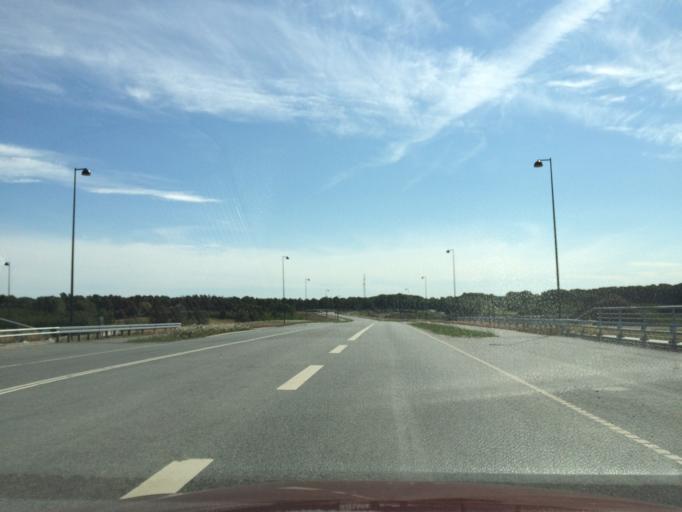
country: DK
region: Central Jutland
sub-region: Silkeborg Kommune
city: Silkeborg
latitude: 56.2011
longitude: 9.5508
